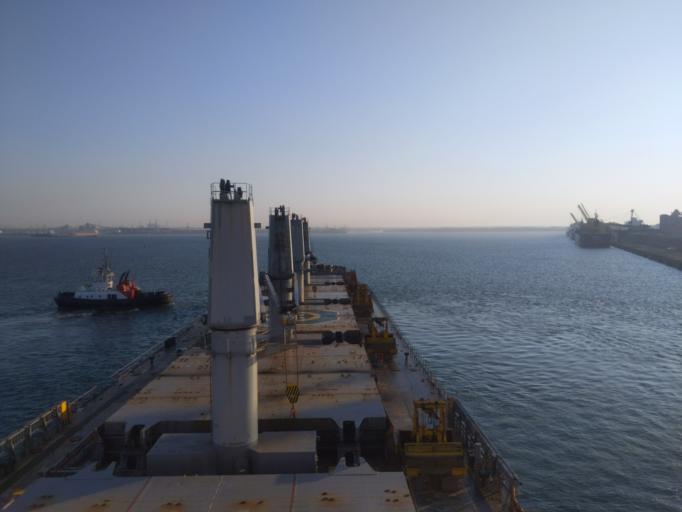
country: ZA
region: KwaZulu-Natal
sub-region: uThungulu District Municipality
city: Richards Bay
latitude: -28.8211
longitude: 32.0459
